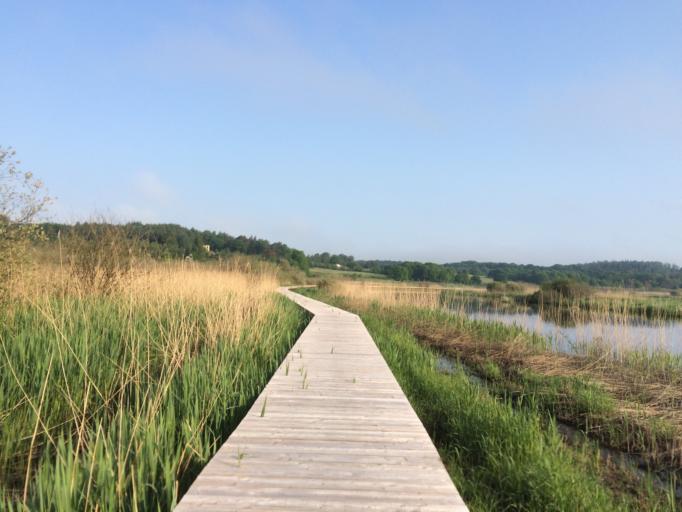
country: DK
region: Central Jutland
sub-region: Silkeborg Kommune
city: Svejbaek
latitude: 56.1960
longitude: 9.6519
